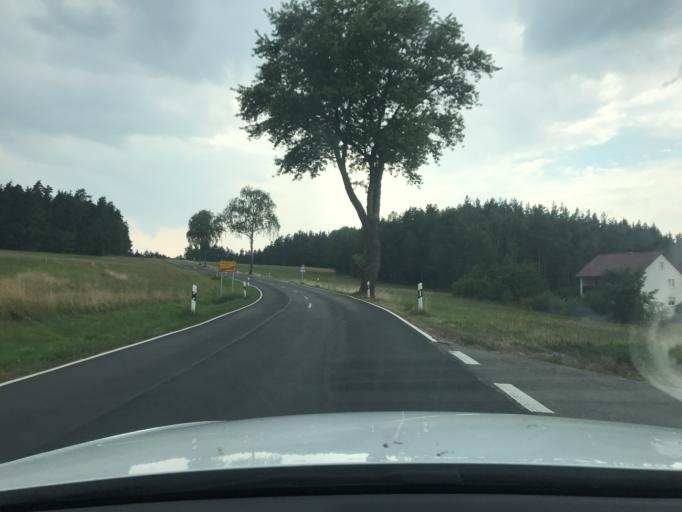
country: DE
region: Bavaria
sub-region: Upper Franconia
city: Prebitz
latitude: 49.7941
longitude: 11.6765
